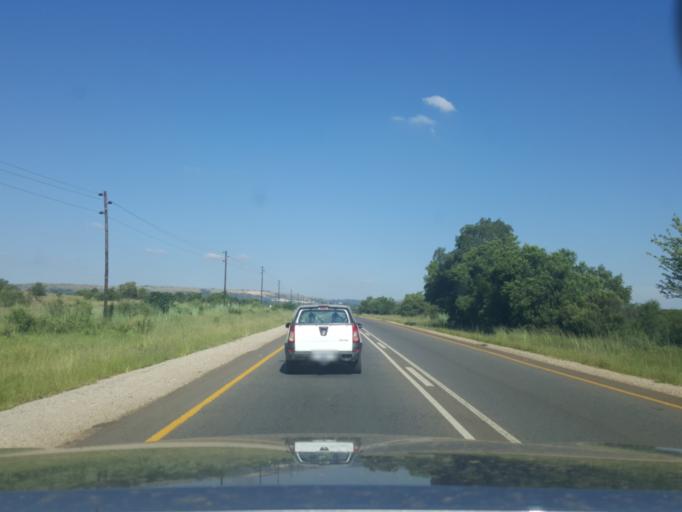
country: ZA
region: Gauteng
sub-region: City of Tshwane Metropolitan Municipality
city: Cullinan
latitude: -25.7551
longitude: 28.3975
